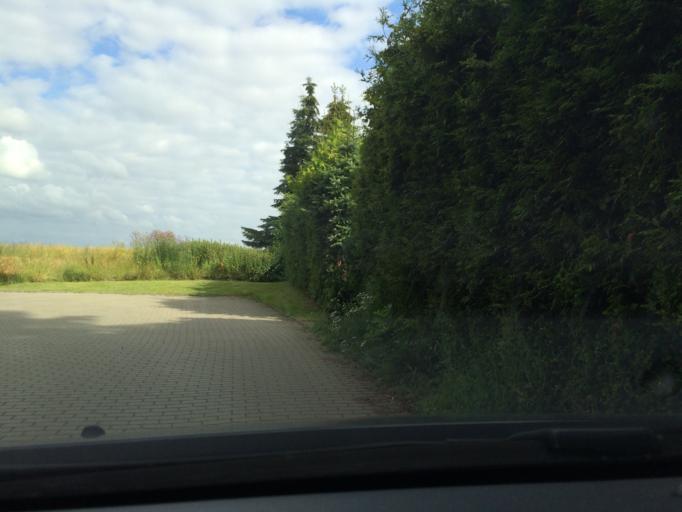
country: DE
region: Mecklenburg-Vorpommern
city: Preetz
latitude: 54.3978
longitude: 12.9801
